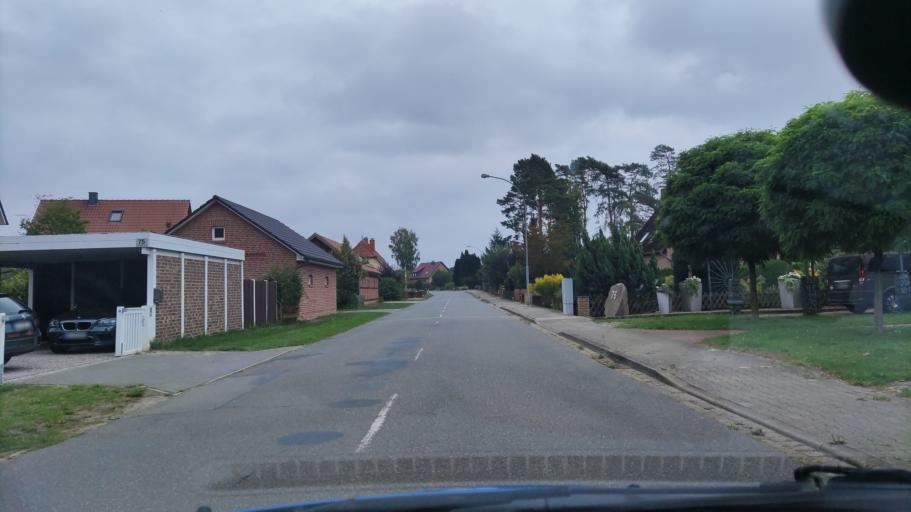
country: DE
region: Lower Saxony
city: Bienenbuttel
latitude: 53.1454
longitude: 10.5036
